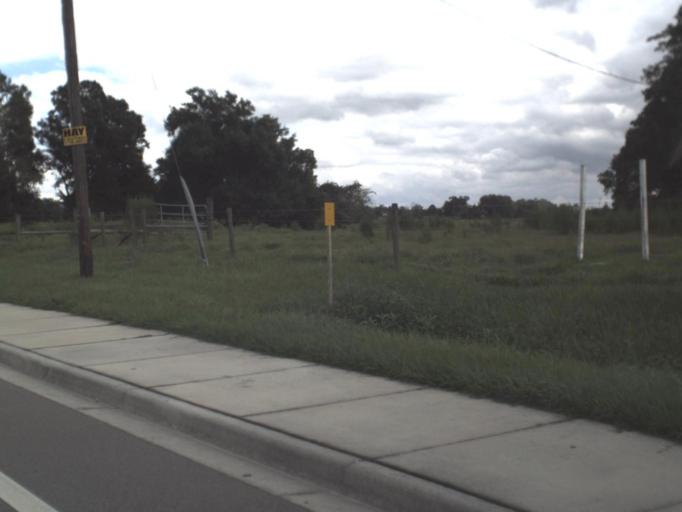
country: US
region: Florida
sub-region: Manatee County
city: Ellenton
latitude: 27.5599
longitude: -82.4437
